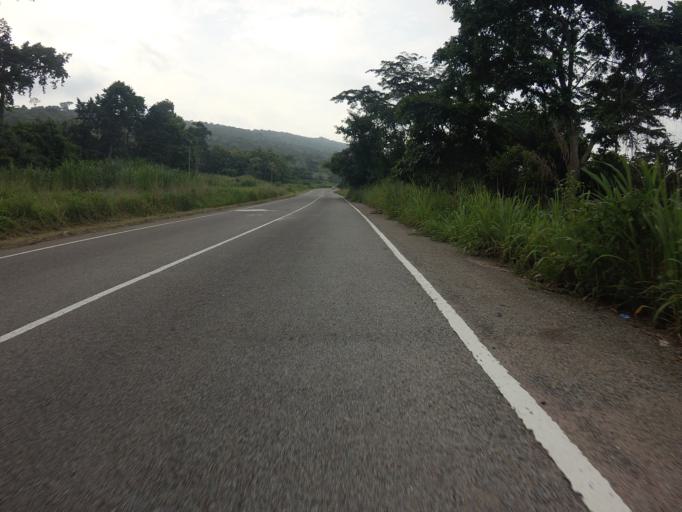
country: GH
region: Volta
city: Ho
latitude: 6.6495
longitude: 0.4702
